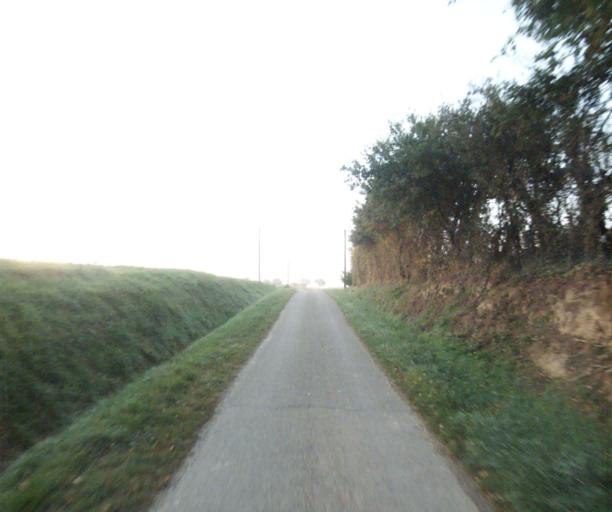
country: FR
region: Midi-Pyrenees
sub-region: Departement du Gers
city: Vic-Fezensac
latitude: 43.7891
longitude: 0.2356
